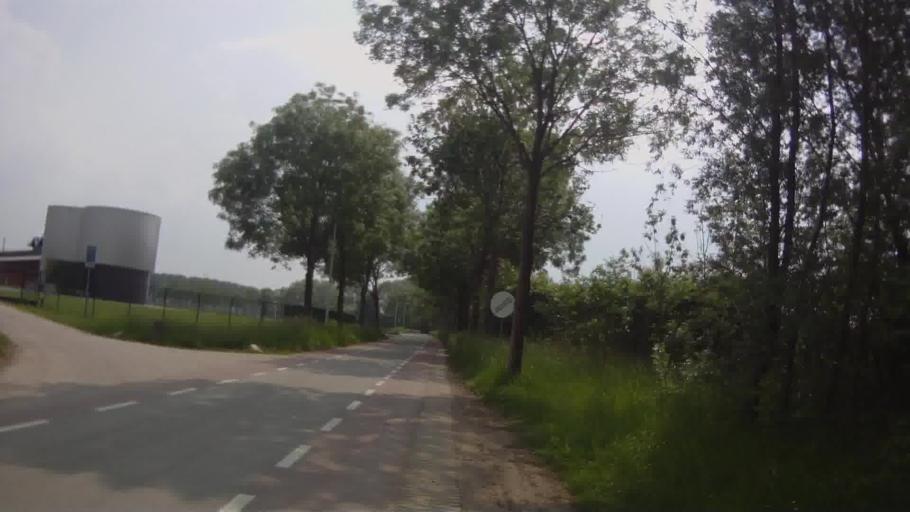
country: NL
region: Utrecht
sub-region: Gemeente Bunnik
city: Bunnik
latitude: 52.0609
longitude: 5.1915
